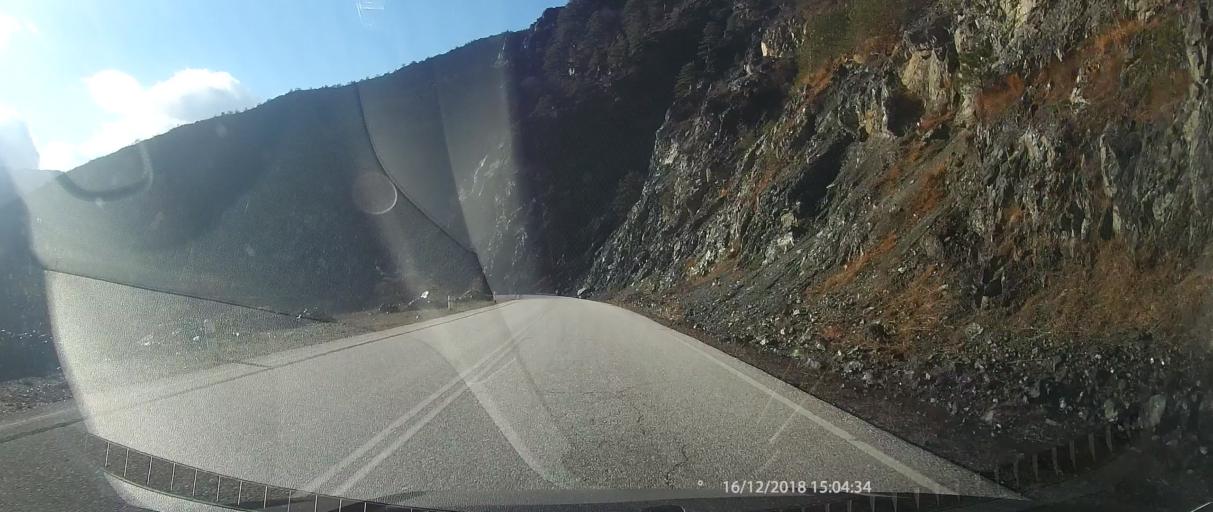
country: GR
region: West Macedonia
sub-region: Nomos Kastorias
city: Nestorio
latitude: 40.2283
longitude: 20.9671
